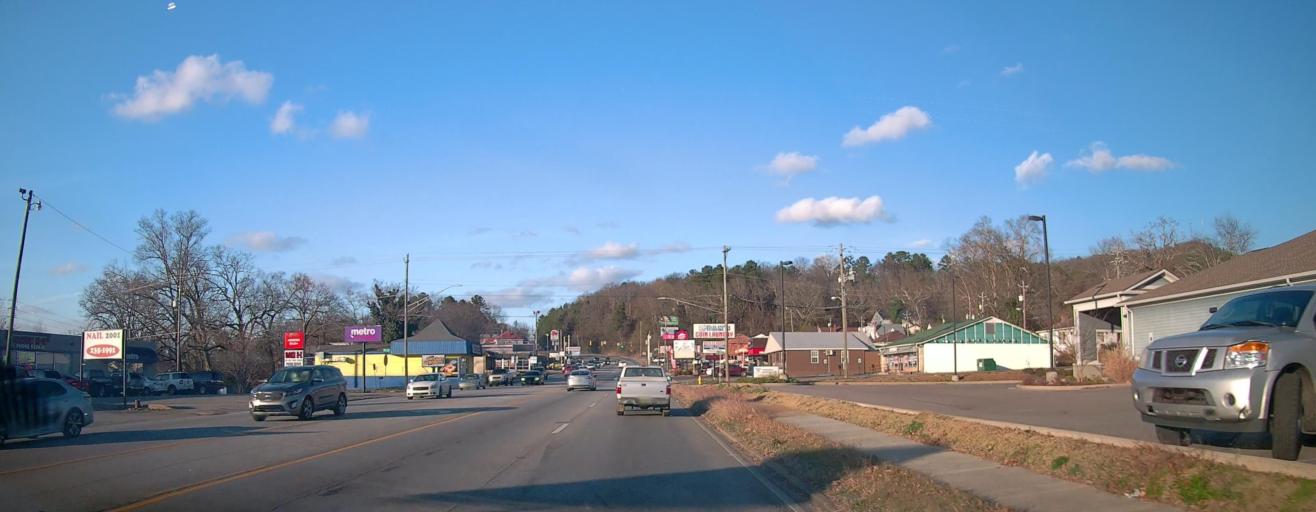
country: US
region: Alabama
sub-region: Calhoun County
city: Anniston
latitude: 33.6712
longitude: -85.8267
